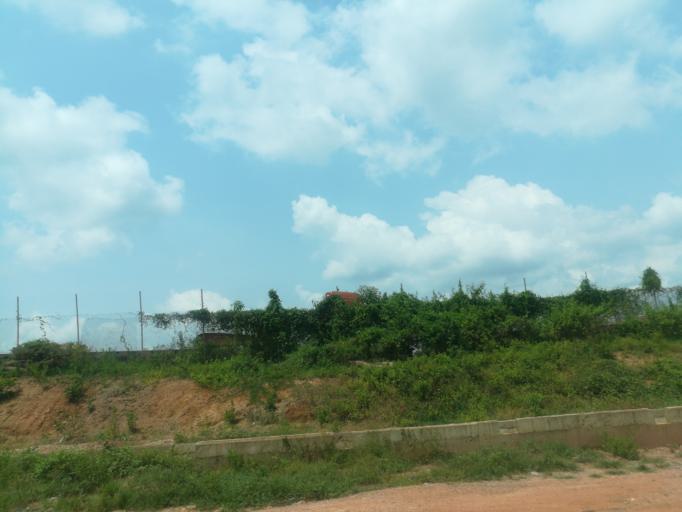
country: NG
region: Oyo
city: Moniya
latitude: 7.4557
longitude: 3.9509
